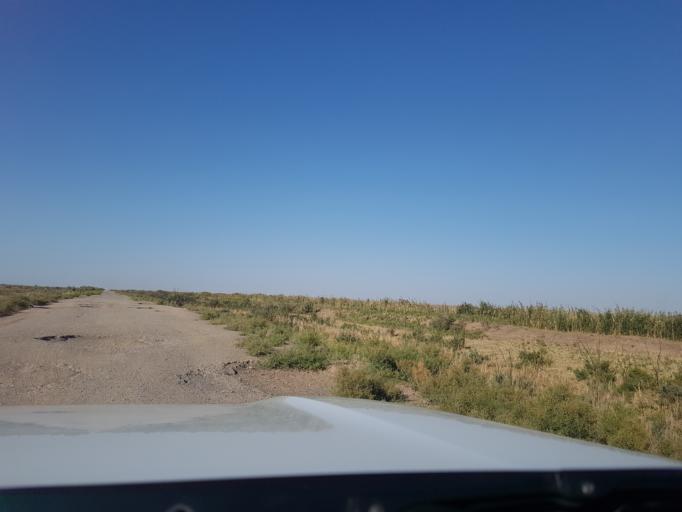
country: IR
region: Razavi Khorasan
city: Sarakhs
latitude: 36.9493
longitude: 61.3796
